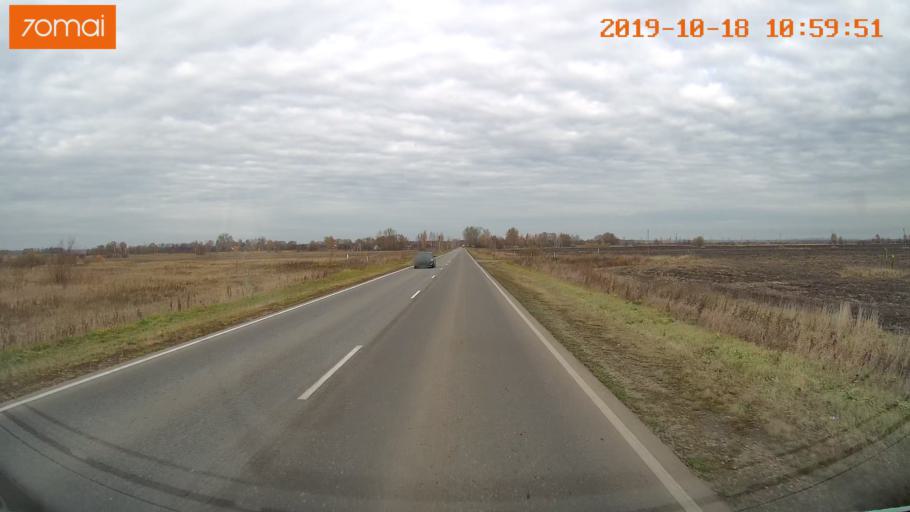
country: RU
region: Tula
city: Yepifan'
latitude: 53.8352
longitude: 38.5551
